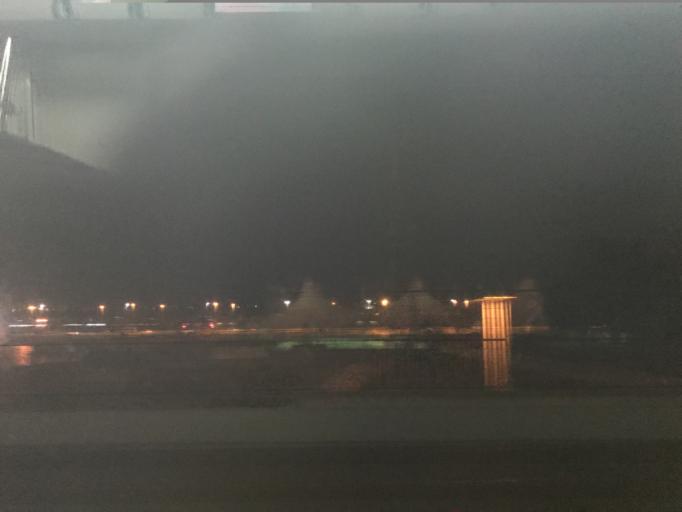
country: TR
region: Istanbul
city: Pendik
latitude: 40.8752
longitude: 29.2480
